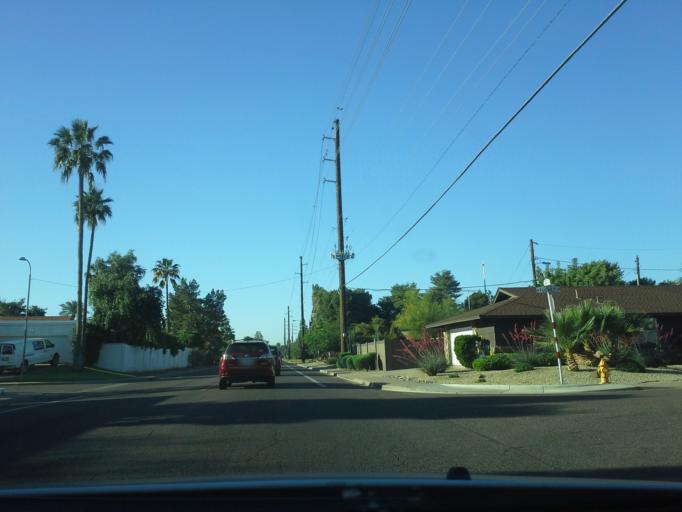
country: US
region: Arizona
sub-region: Maricopa County
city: Phoenix
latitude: 33.5343
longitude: -112.0912
